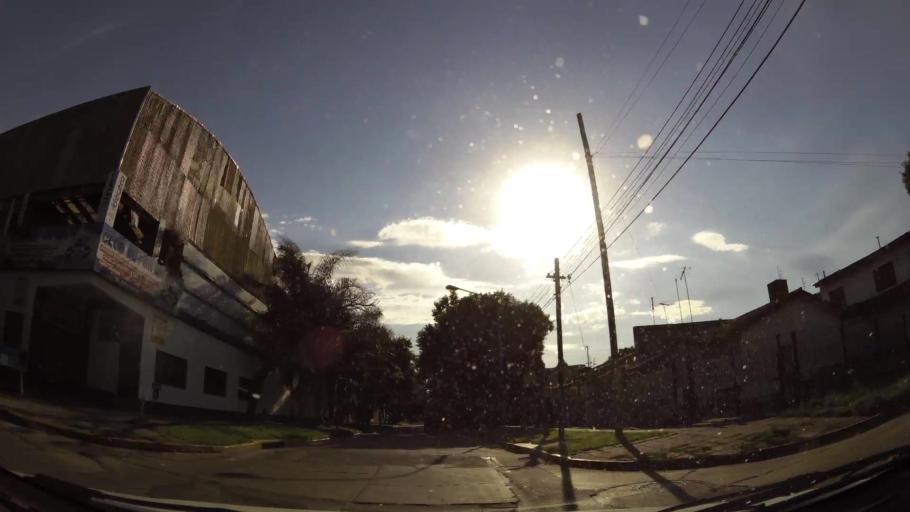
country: AR
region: Buenos Aires
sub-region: Partido de Merlo
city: Merlo
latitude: -34.6717
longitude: -58.7306
